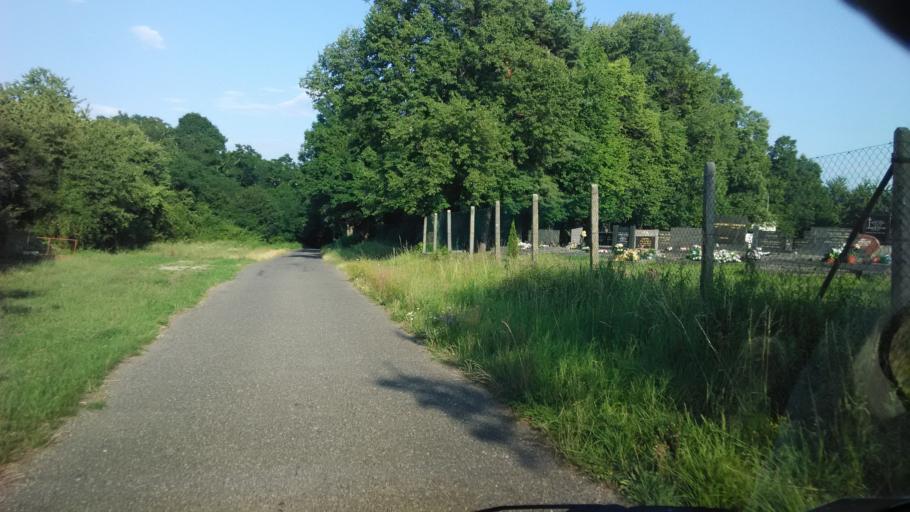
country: SK
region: Nitriansky
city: Levice
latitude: 48.2849
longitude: 18.7023
